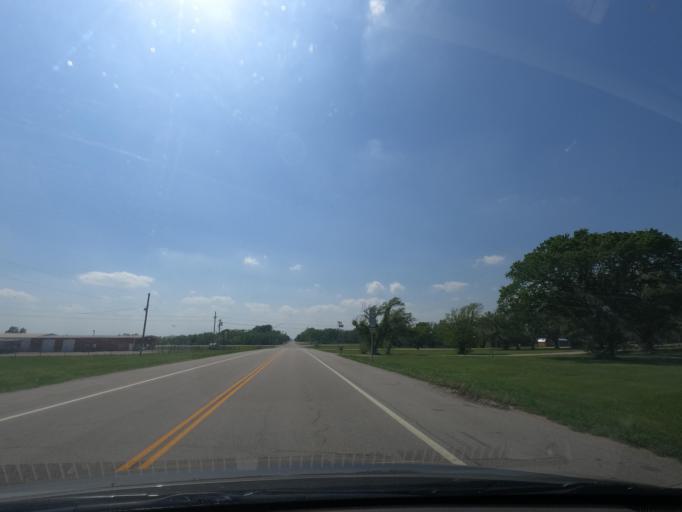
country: US
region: Kansas
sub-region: Butler County
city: Augusta
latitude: 37.6795
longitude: -96.8415
